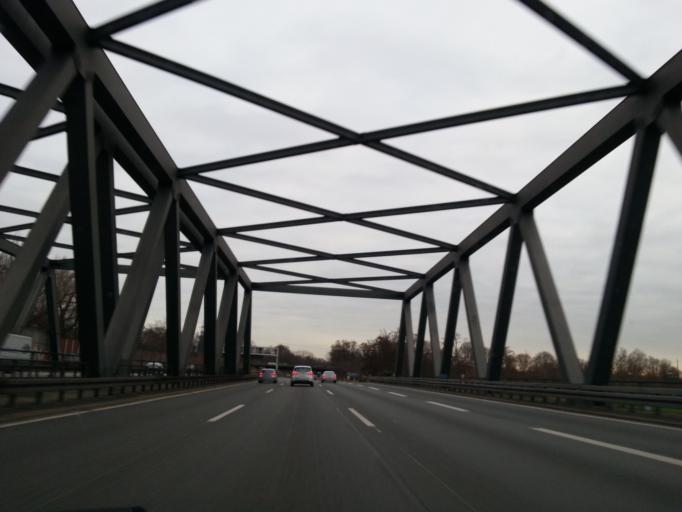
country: DE
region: North Rhine-Westphalia
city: Meiderich
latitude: 51.4782
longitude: 6.8138
